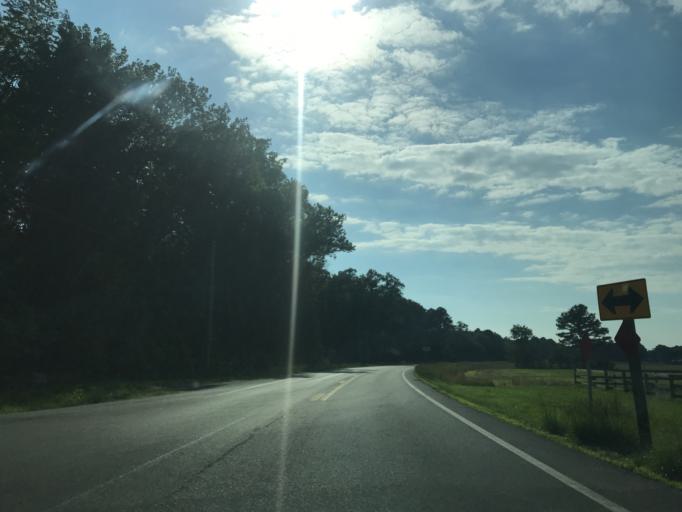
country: US
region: Maryland
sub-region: Wicomico County
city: Hebron
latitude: 38.4594
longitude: -75.6988
